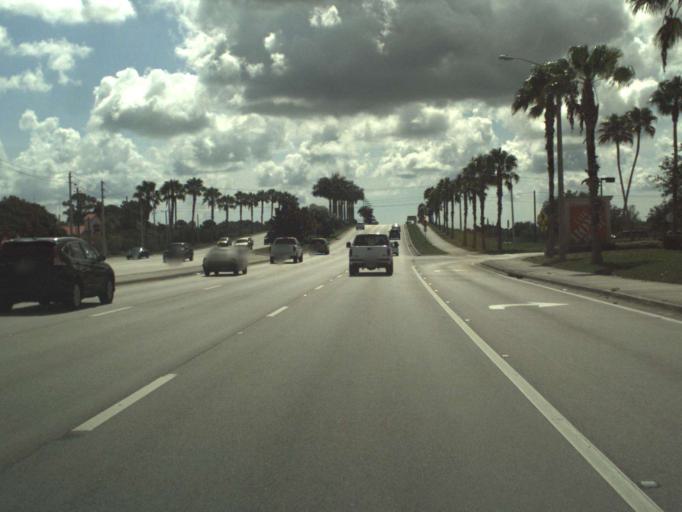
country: US
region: Florida
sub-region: Saint Lucie County
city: River Park
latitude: 27.3177
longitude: -80.3778
